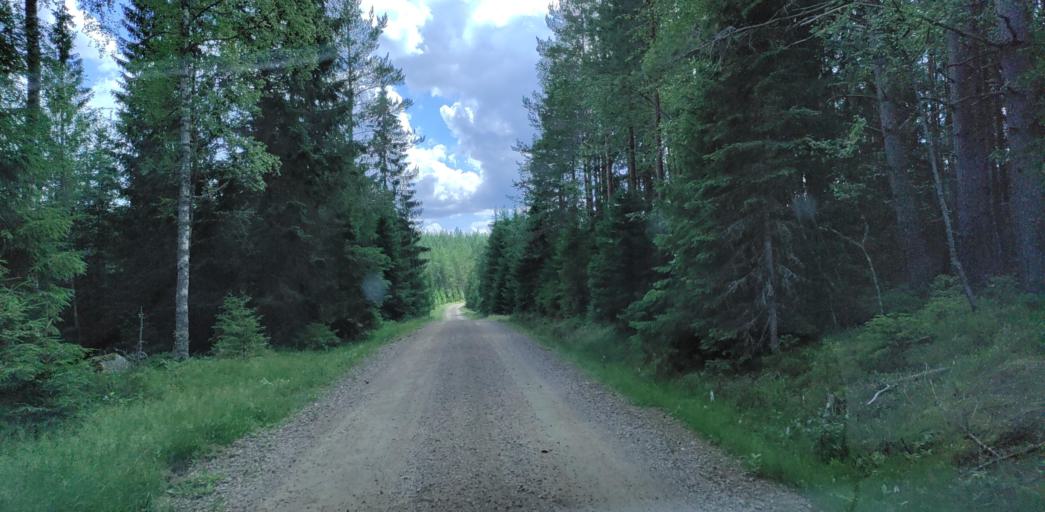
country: SE
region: Vaermland
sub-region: Hagfors Kommun
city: Ekshaerad
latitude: 60.0878
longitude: 13.3457
